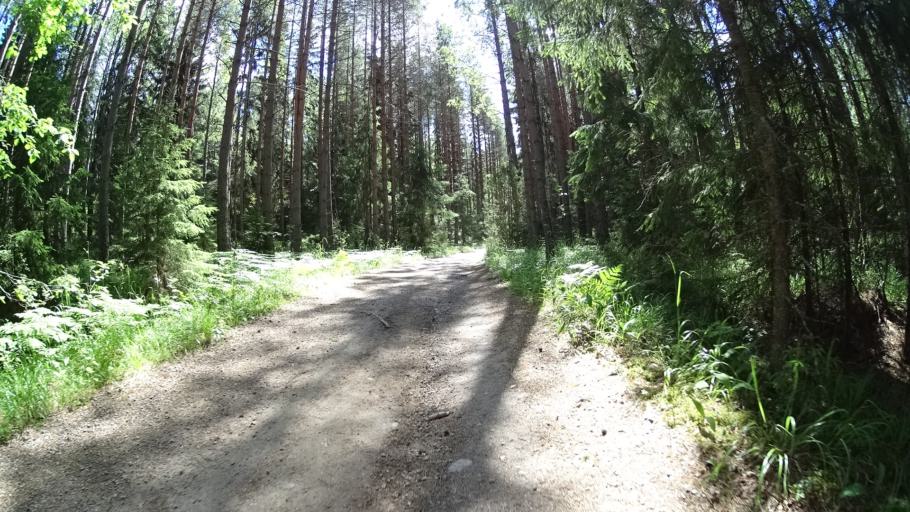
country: FI
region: Uusimaa
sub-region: Helsinki
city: Vihti
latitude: 60.3262
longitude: 24.4864
